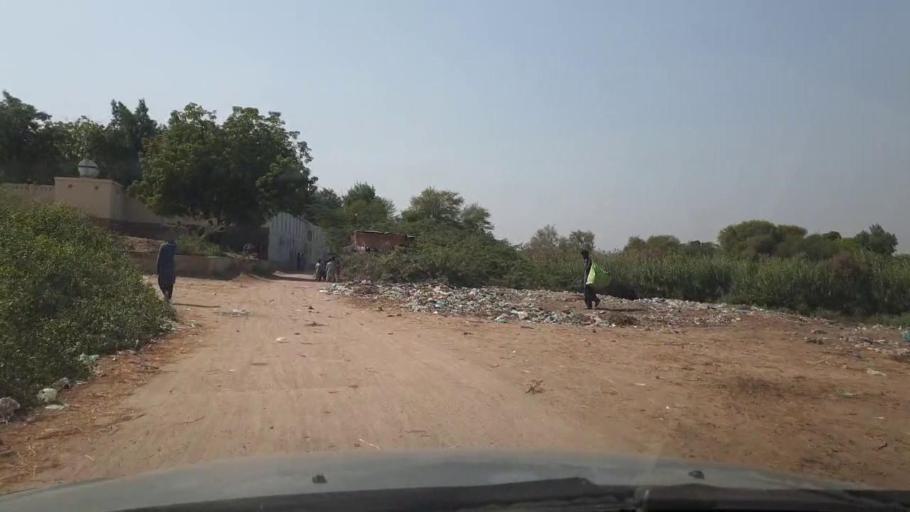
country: PK
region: Sindh
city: Bulri
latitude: 24.8663
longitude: 68.3306
